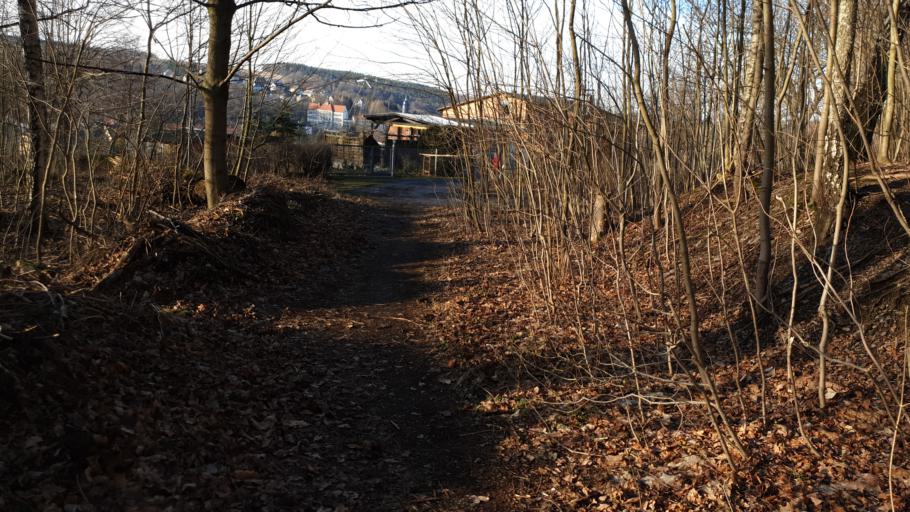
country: DE
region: Saxony
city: Gelenau
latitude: 50.7656
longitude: 12.9781
